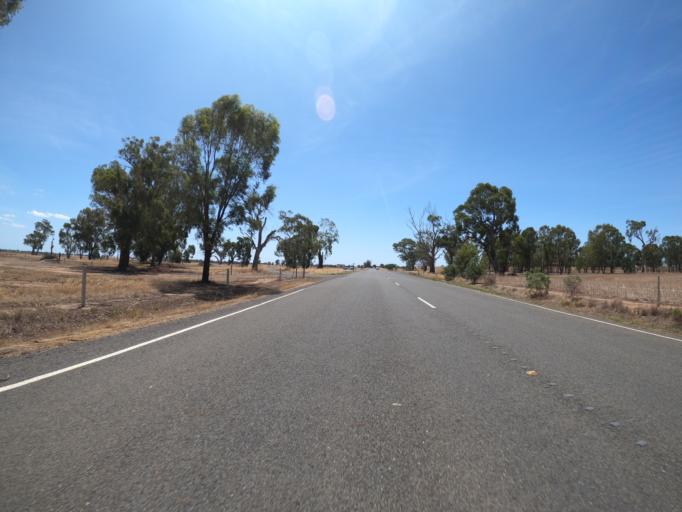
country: AU
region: Victoria
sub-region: Moira
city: Yarrawonga
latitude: -36.1577
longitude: 145.9672
